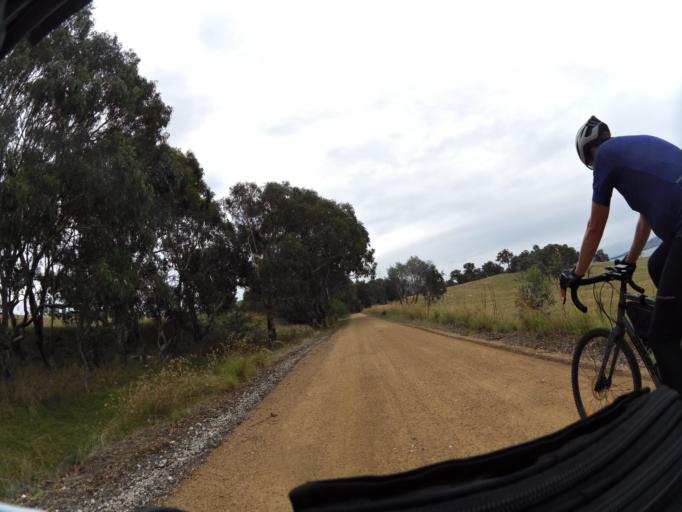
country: AU
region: New South Wales
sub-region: Albury Municipality
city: East Albury
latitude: -36.1988
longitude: 147.0427
